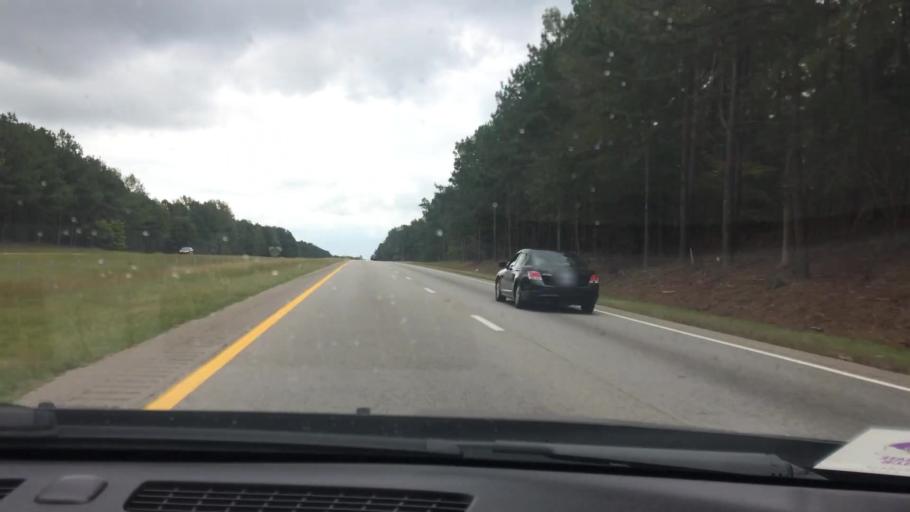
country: US
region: North Carolina
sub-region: Wake County
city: Zebulon
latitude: 35.8098
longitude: -78.2230
